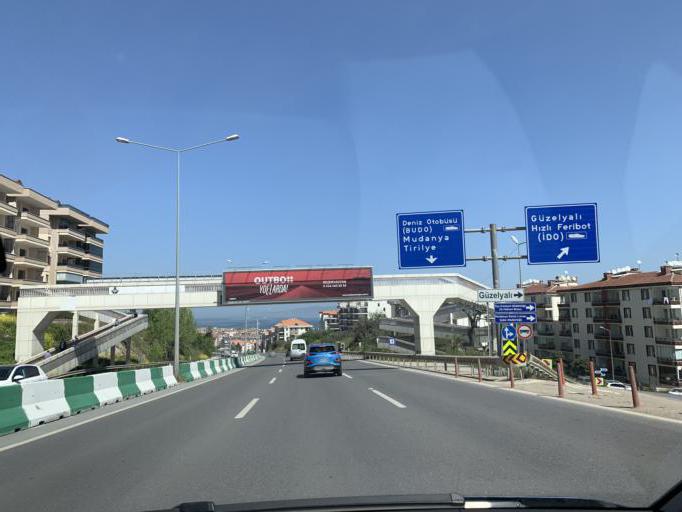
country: TR
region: Bursa
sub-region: Mudanya
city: Mudanya
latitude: 40.3507
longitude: 28.9216
